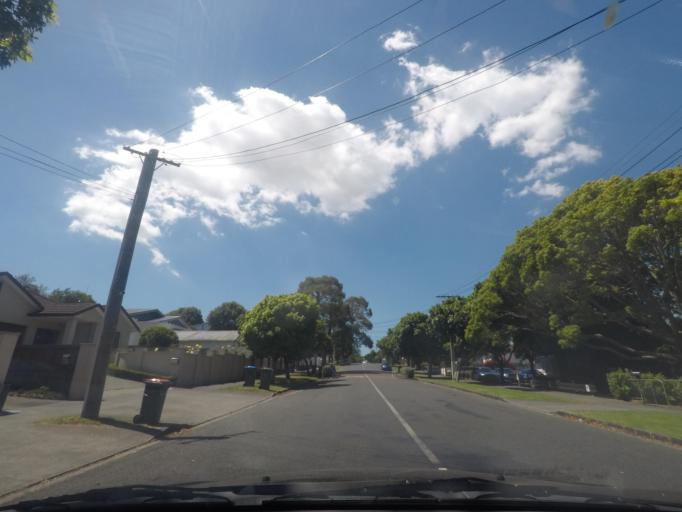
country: NZ
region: Auckland
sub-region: Auckland
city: Auckland
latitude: -36.9080
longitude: 174.7639
